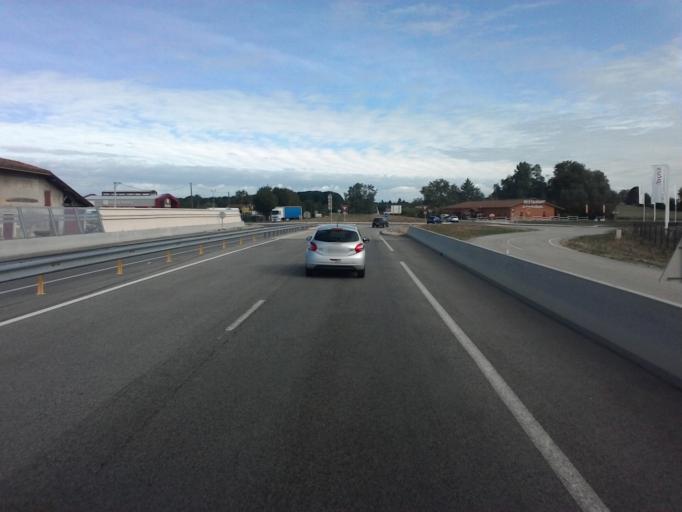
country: FR
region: Rhone-Alpes
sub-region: Departement de l'Ain
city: Montagnat
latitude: 46.1547
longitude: 5.2753
